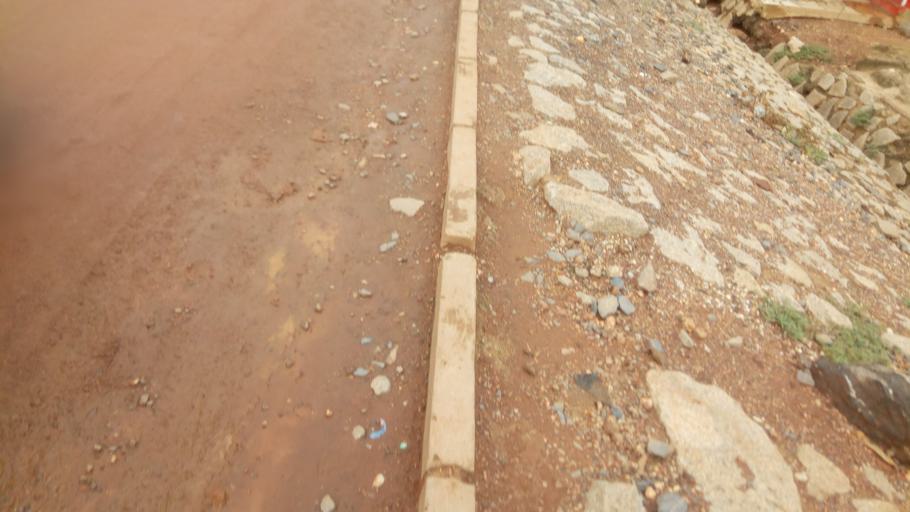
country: GH
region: Ashanti
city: Obuasi
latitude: 6.2108
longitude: -1.6903
